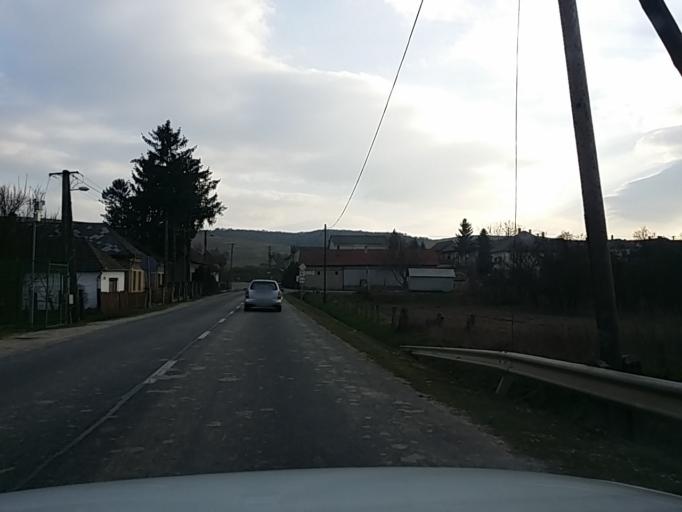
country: HU
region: Borsod-Abauj-Zemplen
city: Ozd
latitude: 48.2826
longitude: 20.3395
